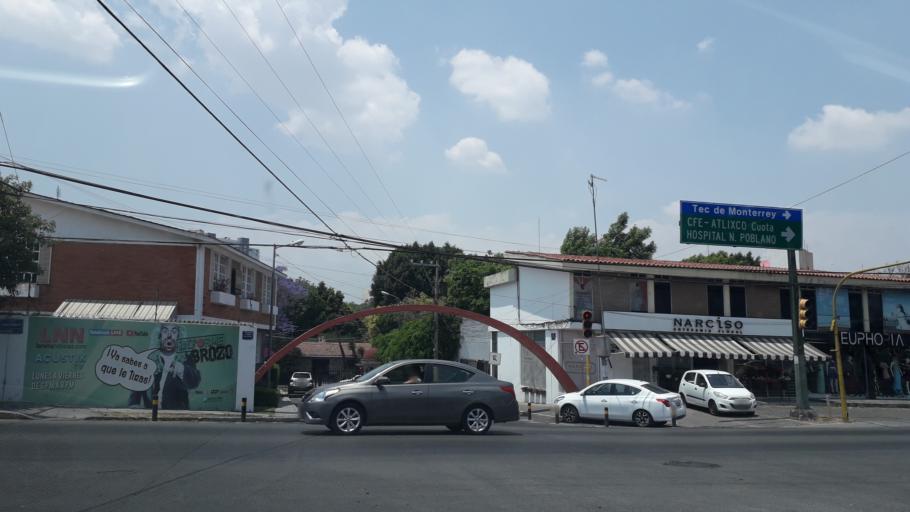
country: MX
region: Puebla
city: Puebla
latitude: 19.0303
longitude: -98.2224
